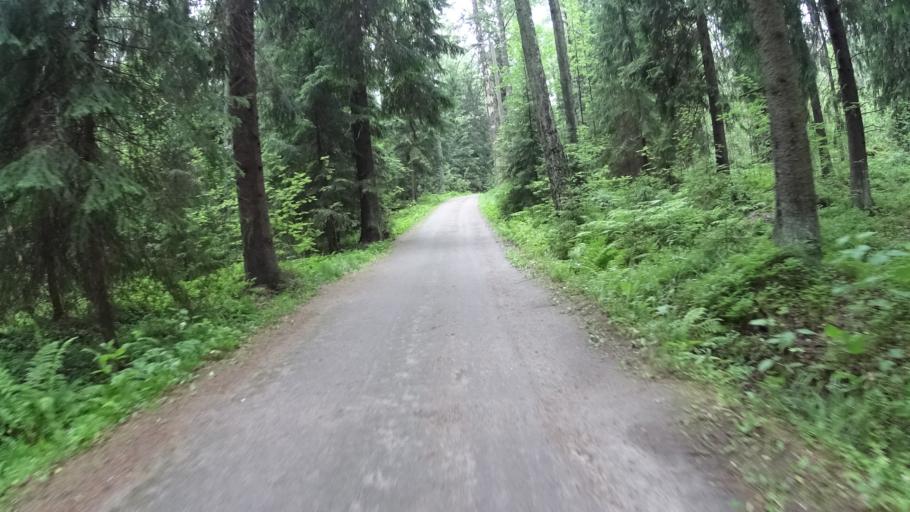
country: FI
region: Uusimaa
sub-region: Helsinki
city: Helsinki
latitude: 60.2636
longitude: 24.9227
